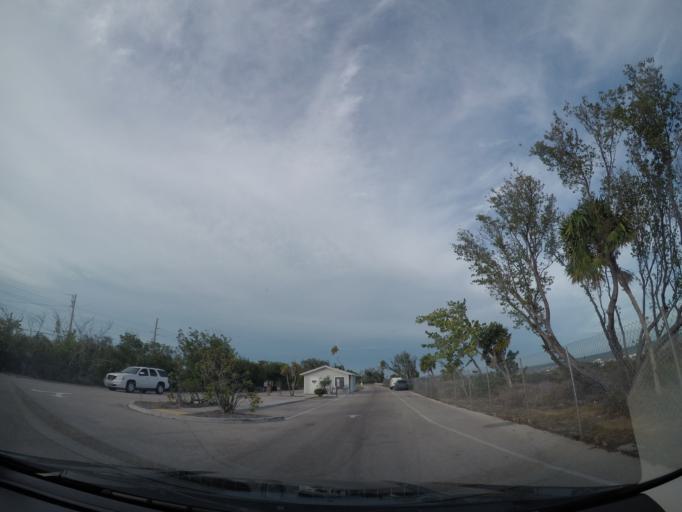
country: US
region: Florida
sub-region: Monroe County
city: Big Pine Key
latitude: 24.6596
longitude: -81.2747
